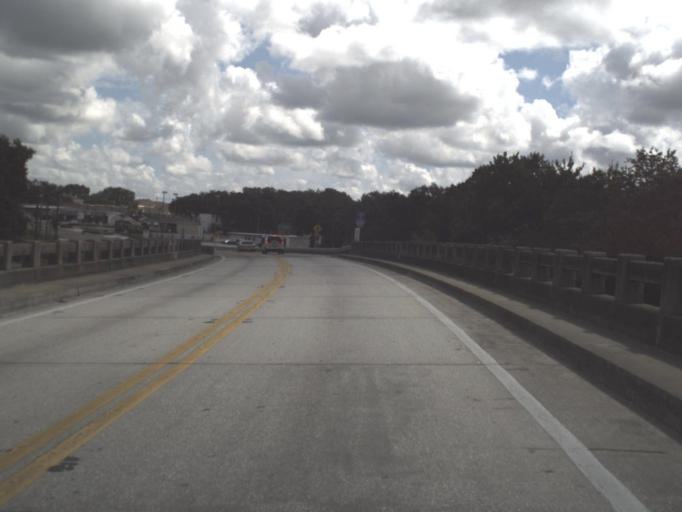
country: US
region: Florida
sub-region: Polk County
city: Polk City
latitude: 28.1792
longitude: -81.8276
